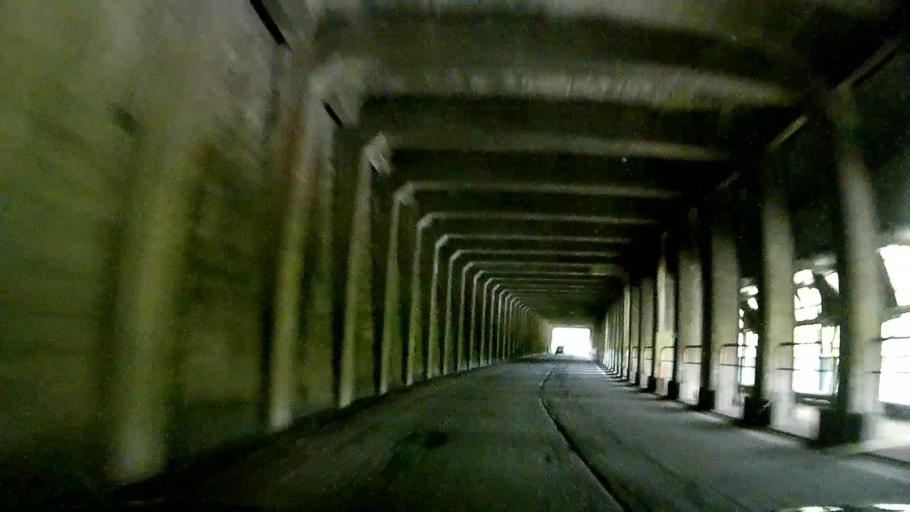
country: JP
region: Niigata
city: Tokamachi
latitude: 36.9972
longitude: 138.6165
